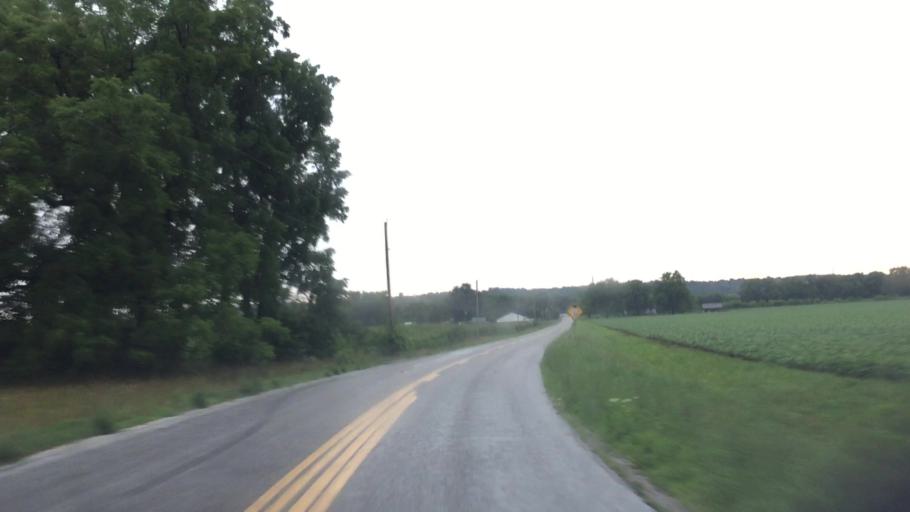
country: US
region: Iowa
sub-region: Lee County
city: Fort Madison
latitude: 40.6119
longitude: -91.2819
